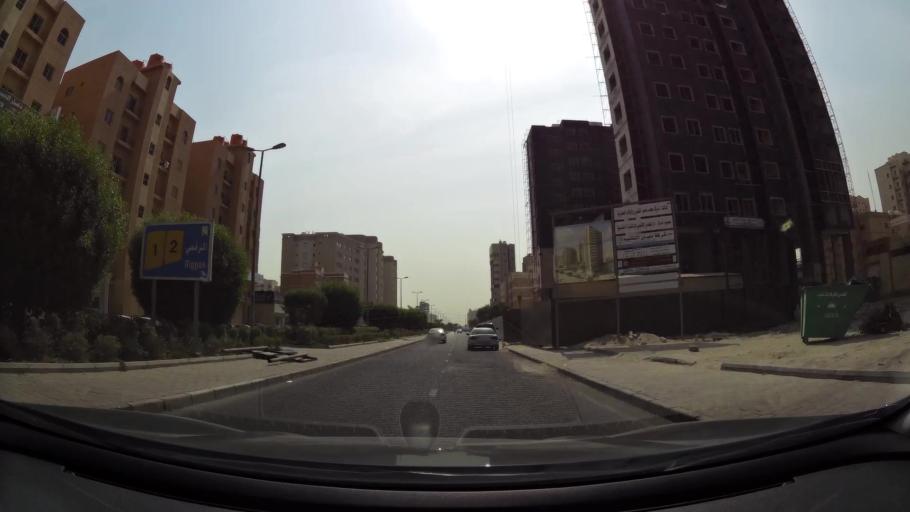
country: KW
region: Al Asimah
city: Ar Rabiyah
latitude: 29.3085
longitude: 47.9146
